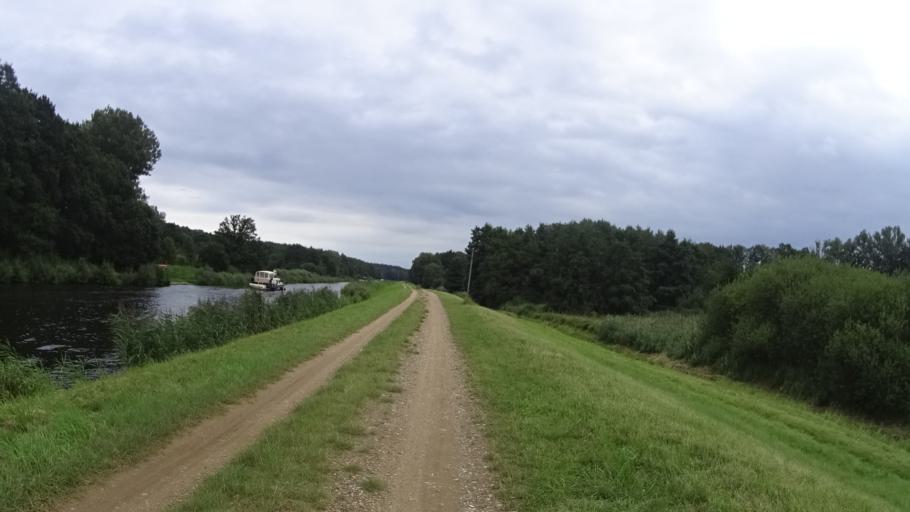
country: DE
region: Schleswig-Holstein
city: Panten
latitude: 53.6599
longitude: 10.6391
